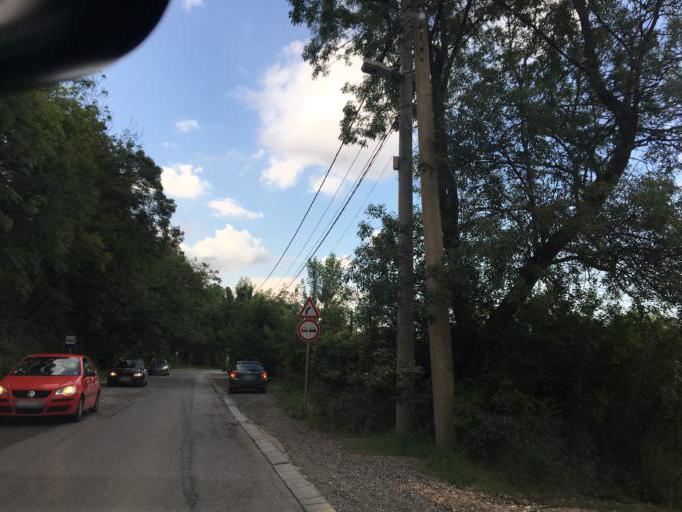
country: BG
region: Sofia-Capital
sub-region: Stolichna Obshtina
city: Sofia
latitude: 42.6322
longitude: 23.3548
